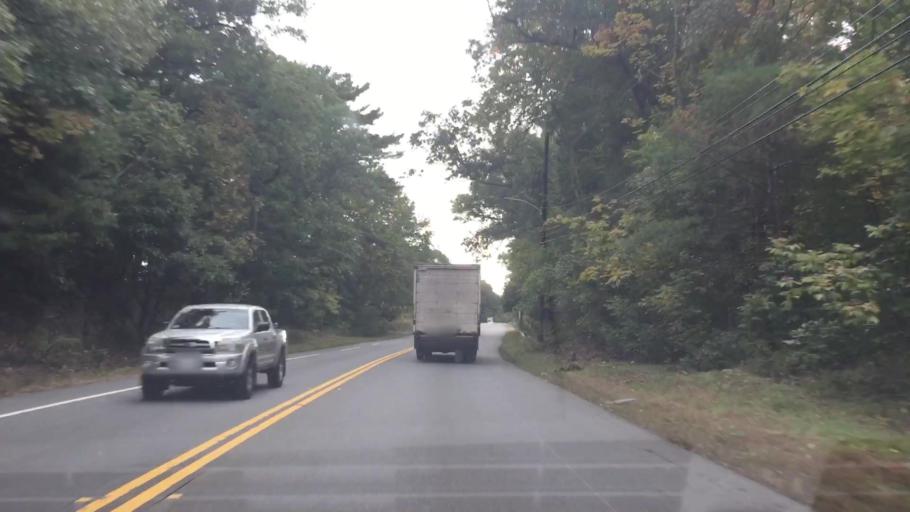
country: US
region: Massachusetts
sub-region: Essex County
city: Middleton
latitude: 42.6146
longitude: -71.0437
